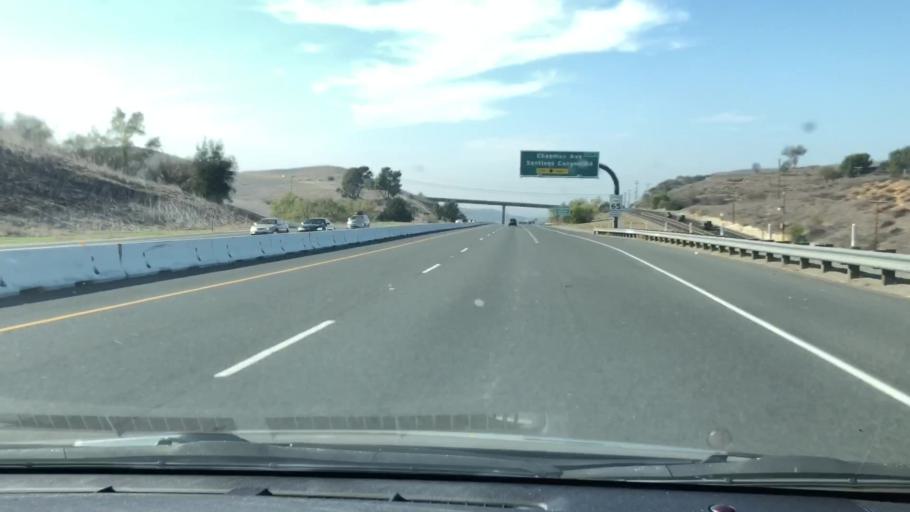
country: US
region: California
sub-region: Orange County
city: North Tustin
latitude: 33.7689
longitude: -117.7379
